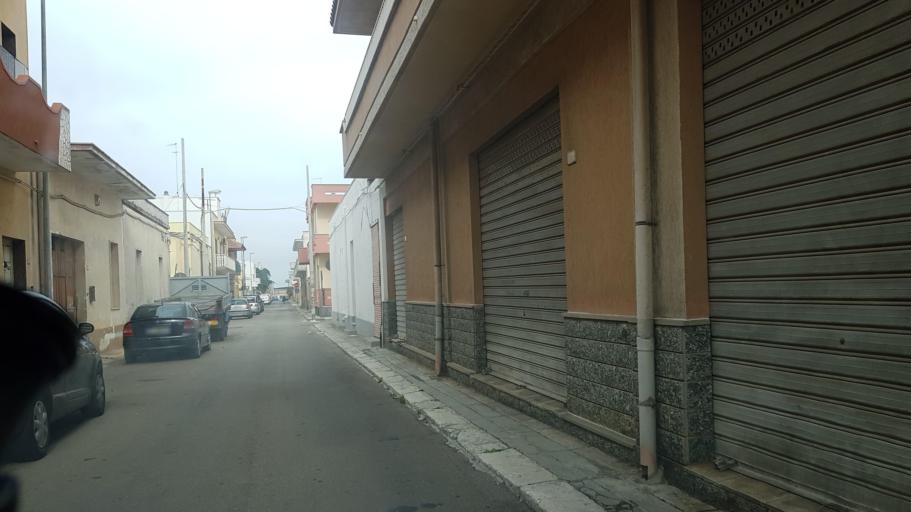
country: IT
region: Apulia
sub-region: Provincia di Brindisi
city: Cellino San Marco
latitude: 40.4731
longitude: 17.9649
